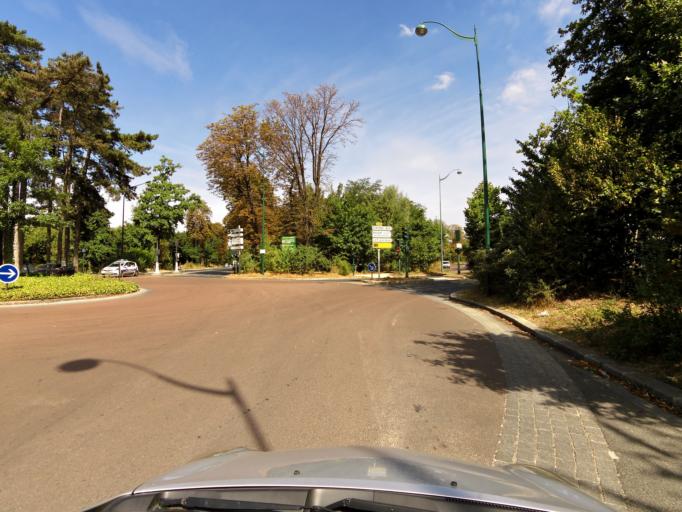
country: FR
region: Ile-de-France
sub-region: Departement du Val-de-Marne
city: Joinville-le-Pont
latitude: 48.8271
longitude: 2.4647
